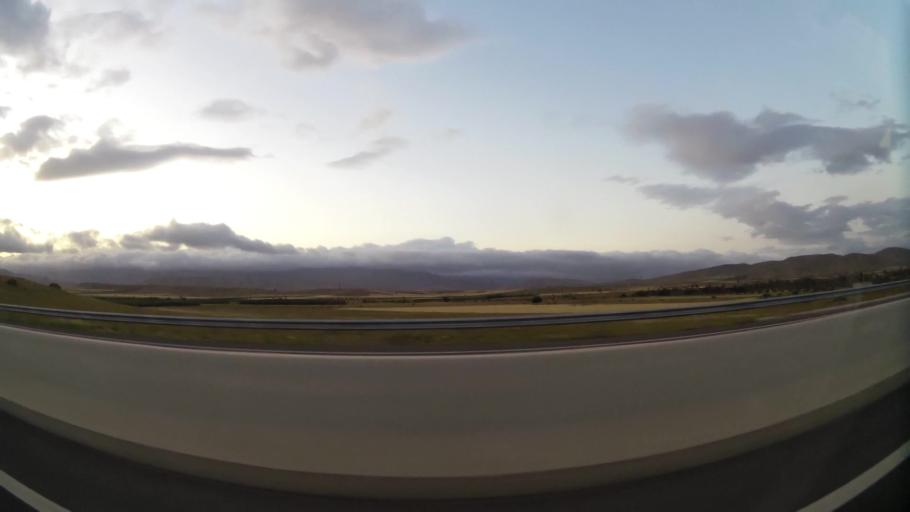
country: MA
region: Oriental
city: El Aioun
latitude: 34.6259
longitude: -2.5105
